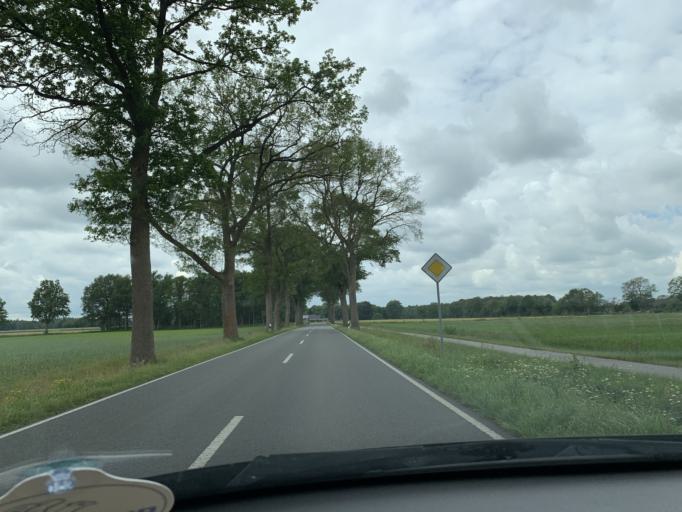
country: DE
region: Lower Saxony
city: Westerstede
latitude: 53.2940
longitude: 7.9912
